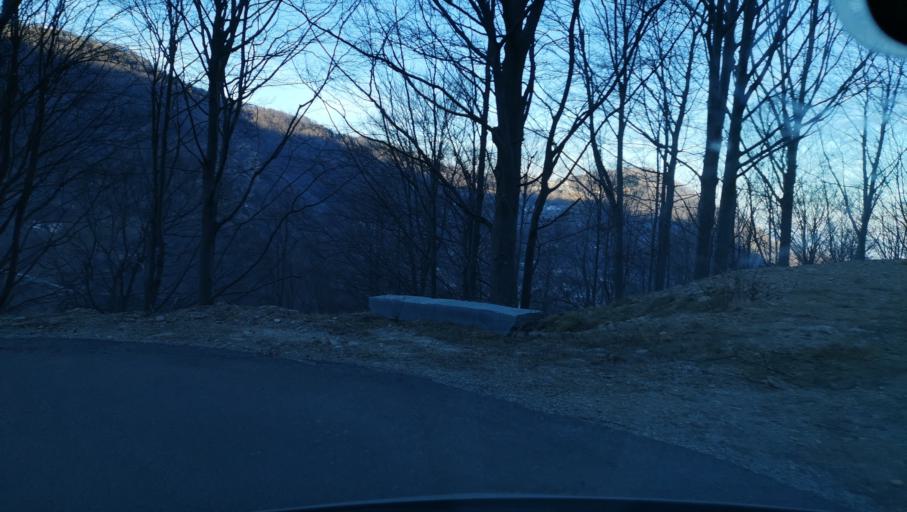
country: IT
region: Piedmont
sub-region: Provincia di Torino
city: Rora
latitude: 44.7824
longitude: 7.1928
